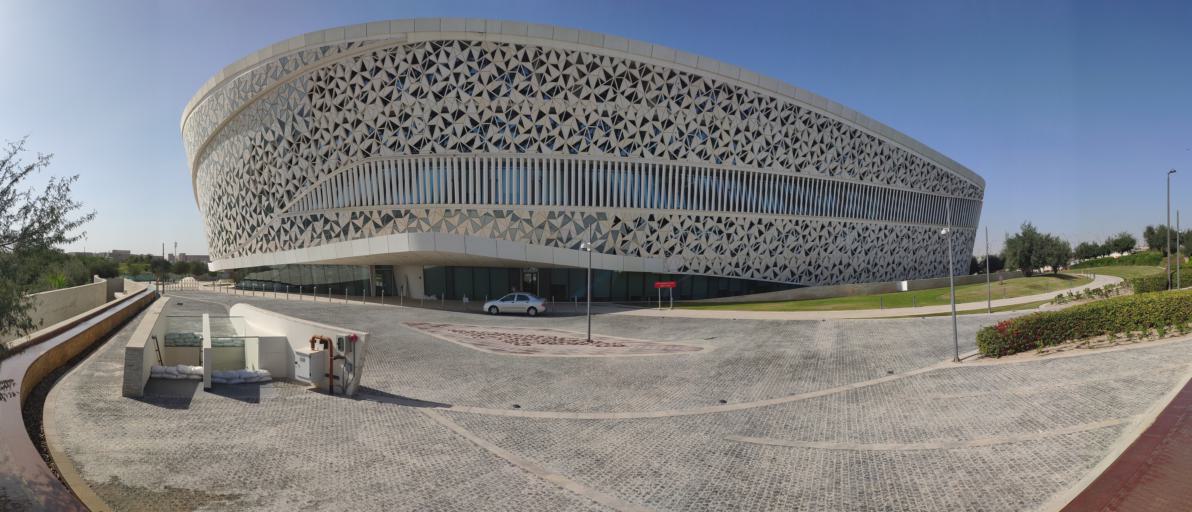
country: QA
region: Baladiyat ar Rayyan
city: Ar Rayyan
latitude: 25.3163
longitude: 51.4477
